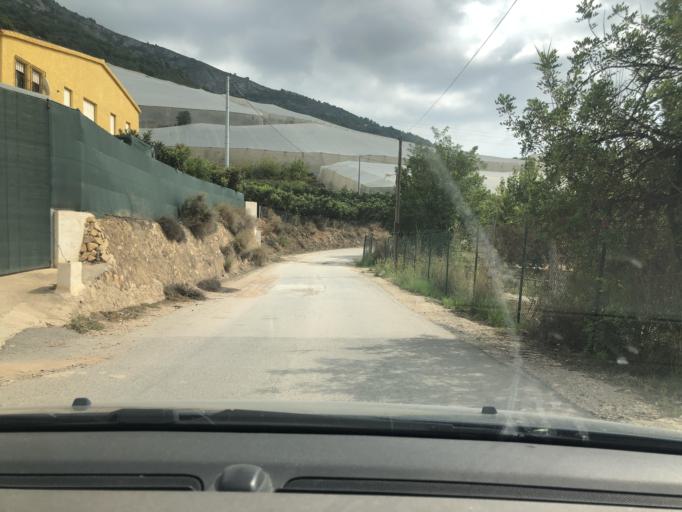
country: ES
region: Valencia
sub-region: Provincia de Alicante
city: Callosa d'En Sarria
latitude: 38.6552
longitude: -0.0936
